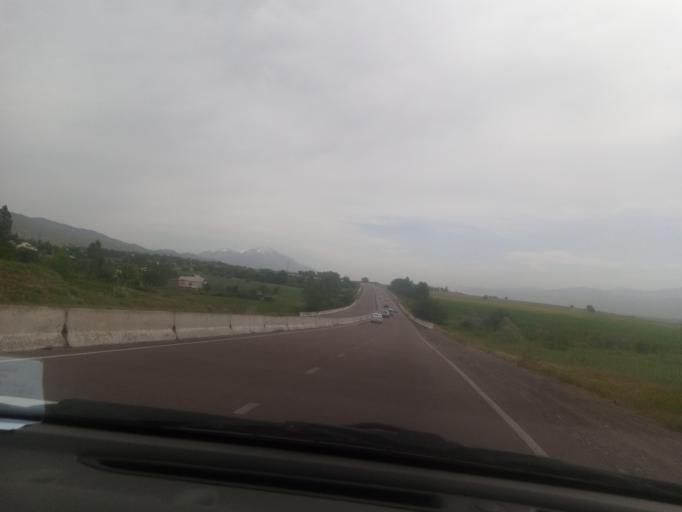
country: UZ
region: Toshkent
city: Angren
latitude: 40.9384
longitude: 69.8986
